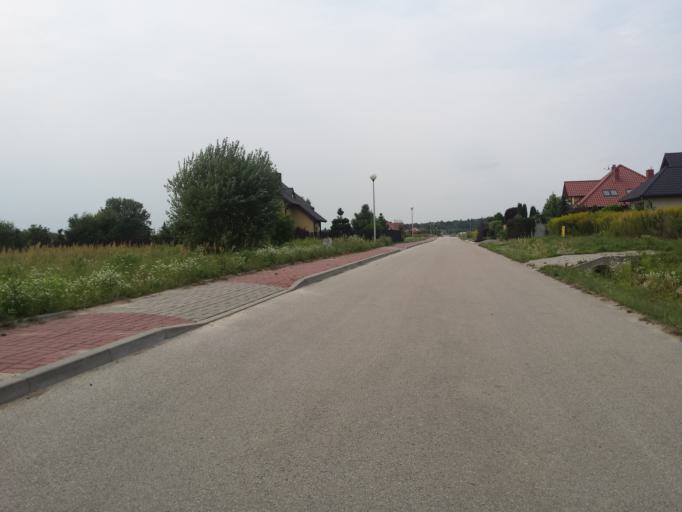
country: PL
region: Swietokrzyskie
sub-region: Powiat kielecki
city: Morawica
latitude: 50.7697
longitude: 20.6332
